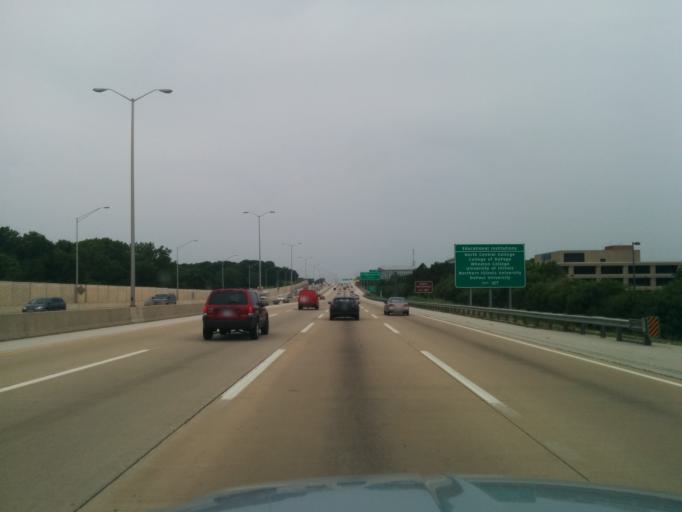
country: US
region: Illinois
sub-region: DuPage County
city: Lisle
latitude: 41.8060
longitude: -88.1061
